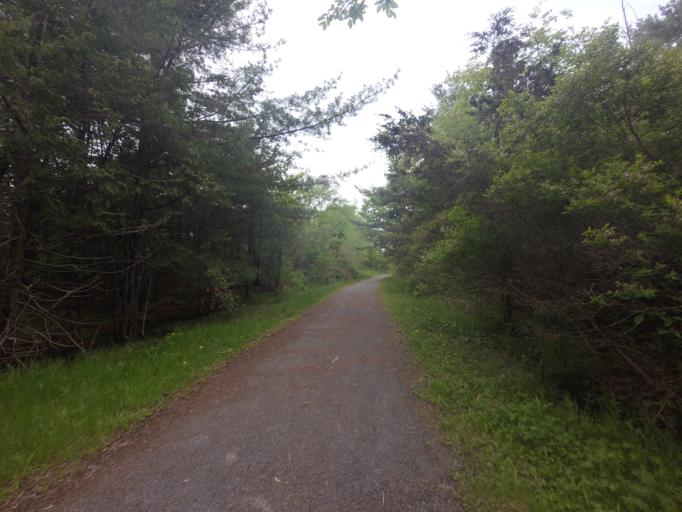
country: CA
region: Ontario
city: Kingston
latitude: 44.2817
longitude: -76.5637
